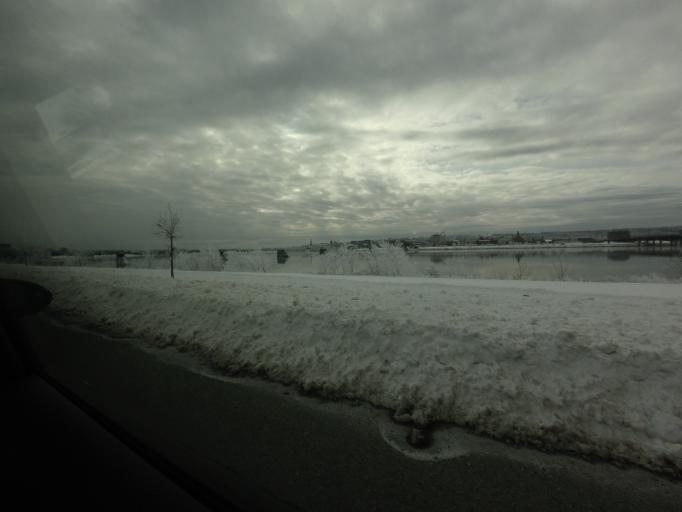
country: CA
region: New Brunswick
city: Fredericton
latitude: 45.9702
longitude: -66.6375
